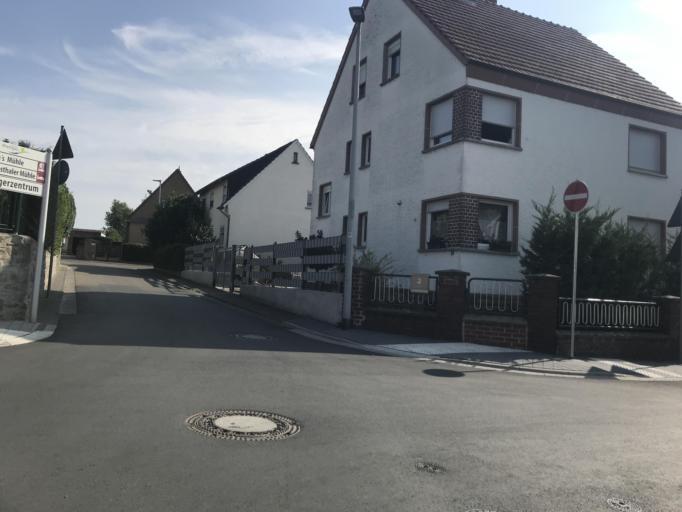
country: DE
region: Rheinland-Pfalz
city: Oestrich-Winkel
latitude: 50.0091
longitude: 8.0243
